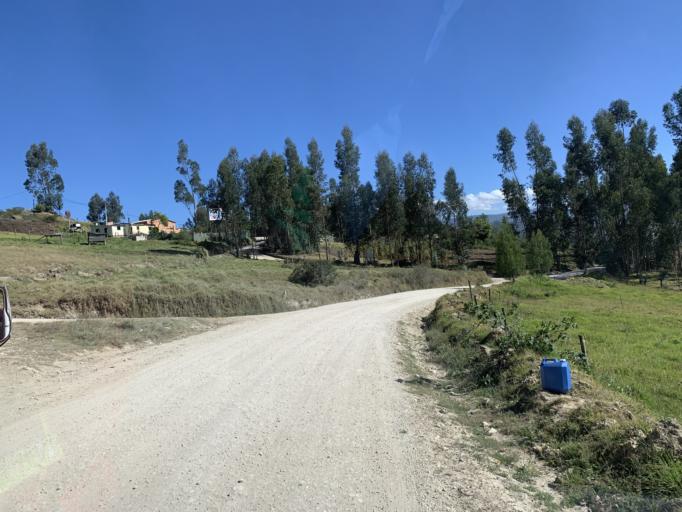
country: CO
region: Boyaca
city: Tuta
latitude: 5.7104
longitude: -73.1539
